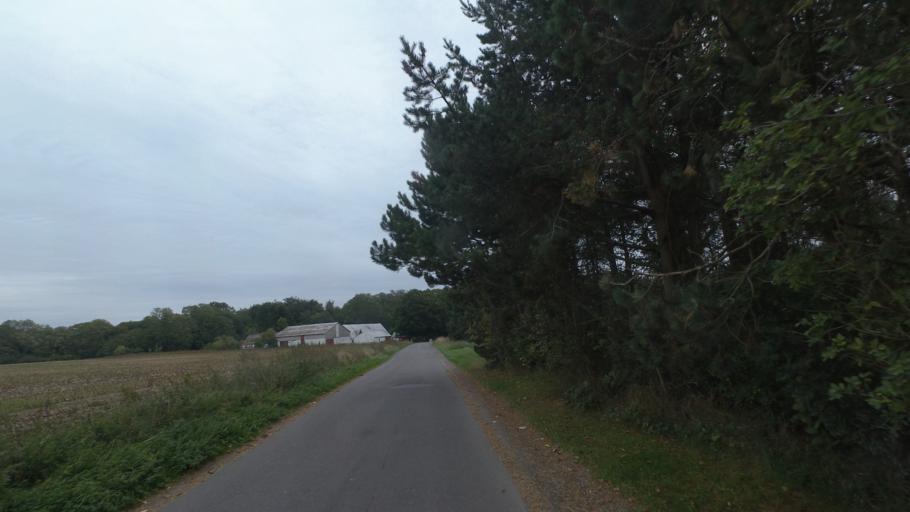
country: DK
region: Capital Region
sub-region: Bornholm Kommune
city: Akirkeby
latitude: 55.0064
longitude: 14.9918
